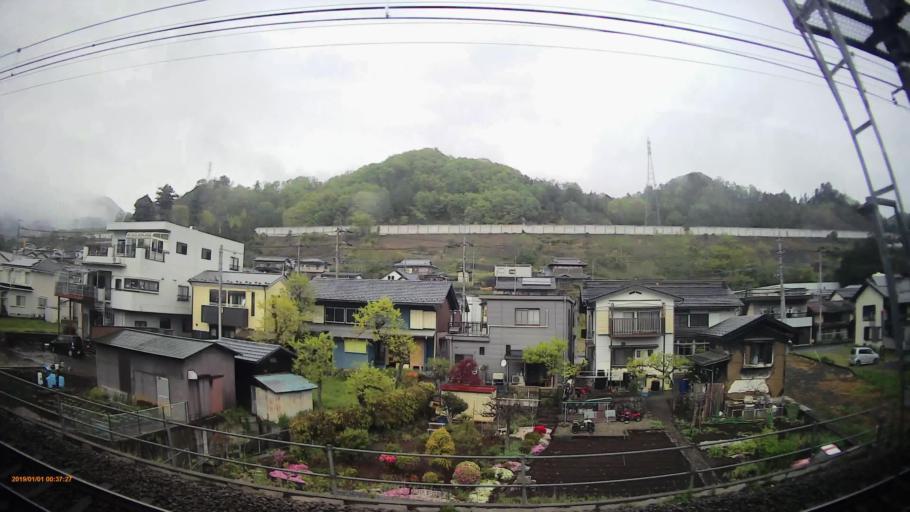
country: JP
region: Yamanashi
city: Otsuki
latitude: 35.6083
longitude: 139.0082
